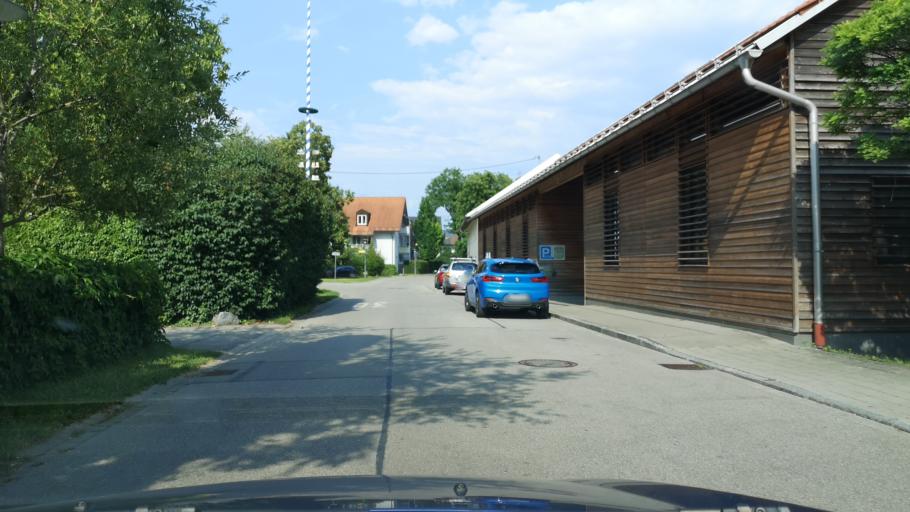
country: DE
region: Bavaria
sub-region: Upper Bavaria
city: Kirchheim bei Muenchen
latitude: 48.1763
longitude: 11.7427
